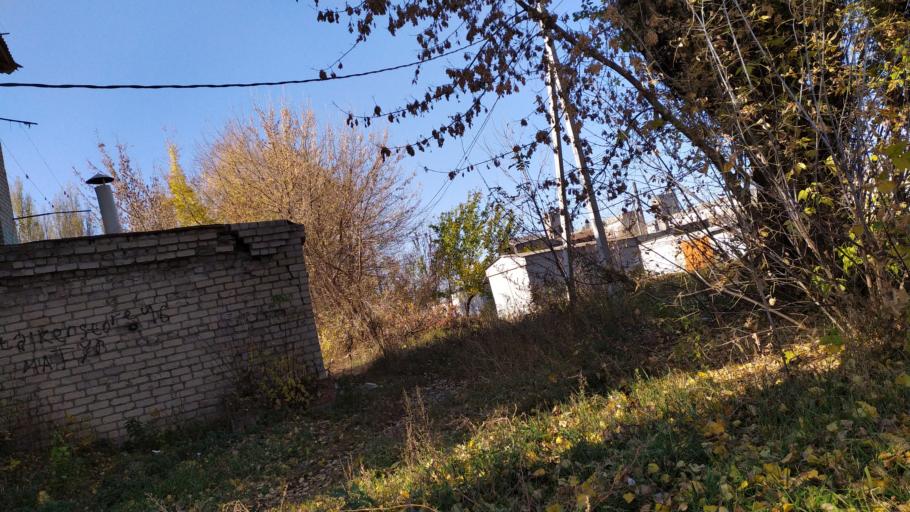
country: RU
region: Kursk
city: Kursk
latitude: 51.6496
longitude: 36.1522
